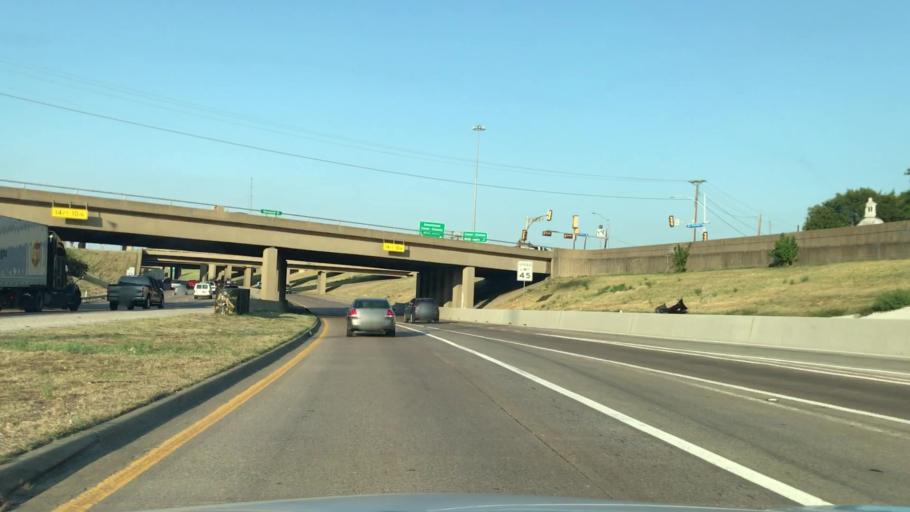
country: US
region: Texas
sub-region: Dallas County
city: Dallas
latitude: 32.7744
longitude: -96.7882
